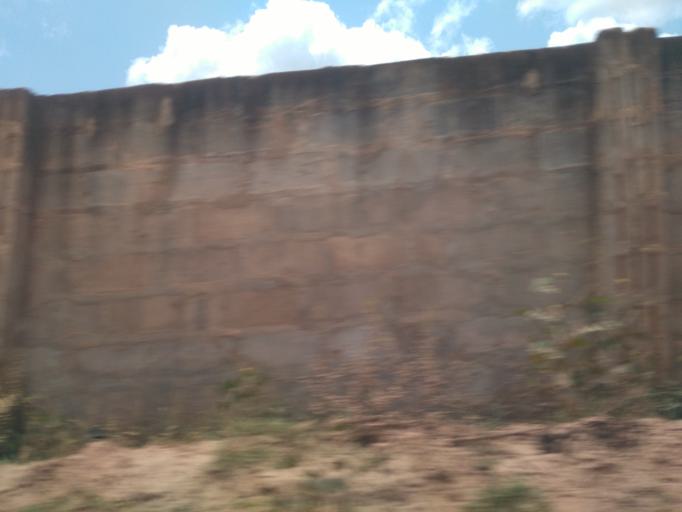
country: TZ
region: Dar es Salaam
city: Dar es Salaam
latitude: -6.8410
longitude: 39.3401
